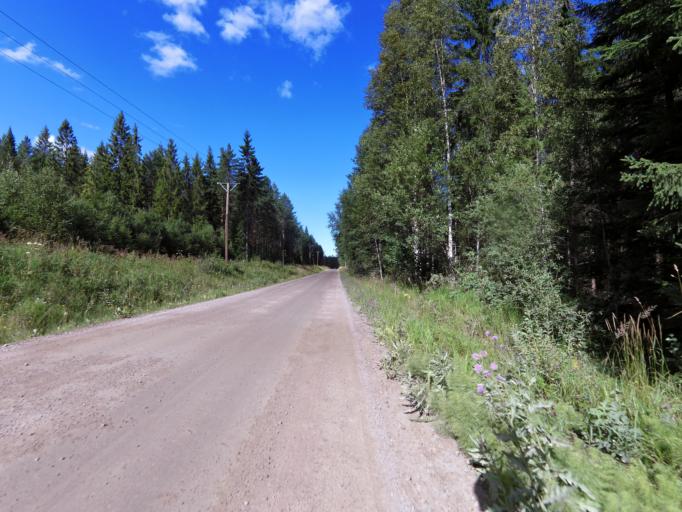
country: SE
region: Gaevleborg
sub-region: Hofors Kommun
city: Hofors
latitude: 60.5077
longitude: 16.3164
